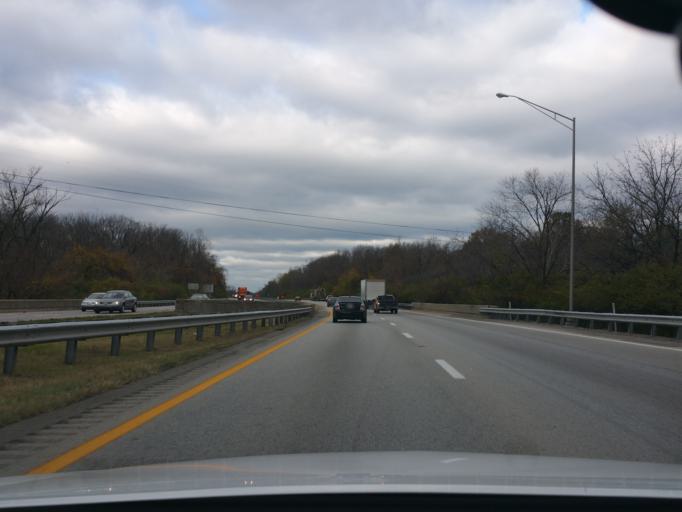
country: US
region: Kentucky
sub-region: Jefferson County
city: Saint Matthews
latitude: 38.2377
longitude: -85.6638
